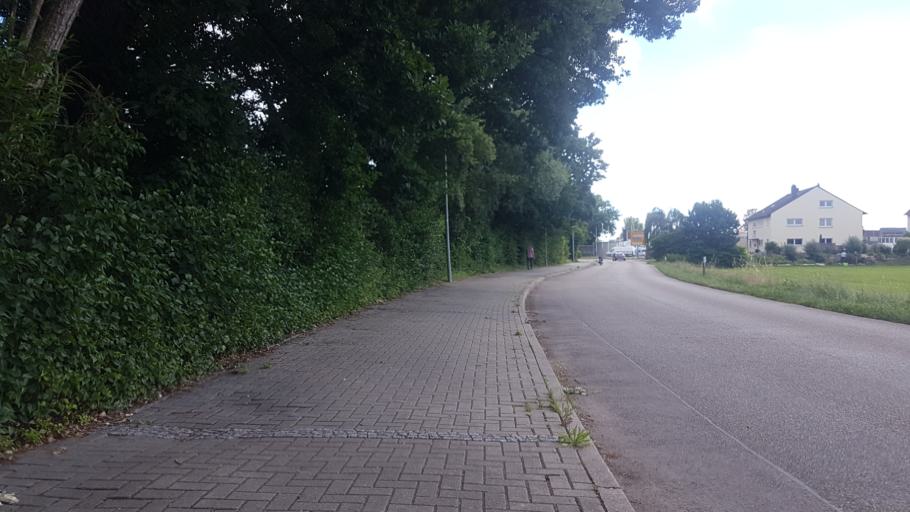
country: DE
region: Bavaria
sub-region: Regierungsbezirk Mittelfranken
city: Gunzenhausen
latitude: 49.1271
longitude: 10.7454
